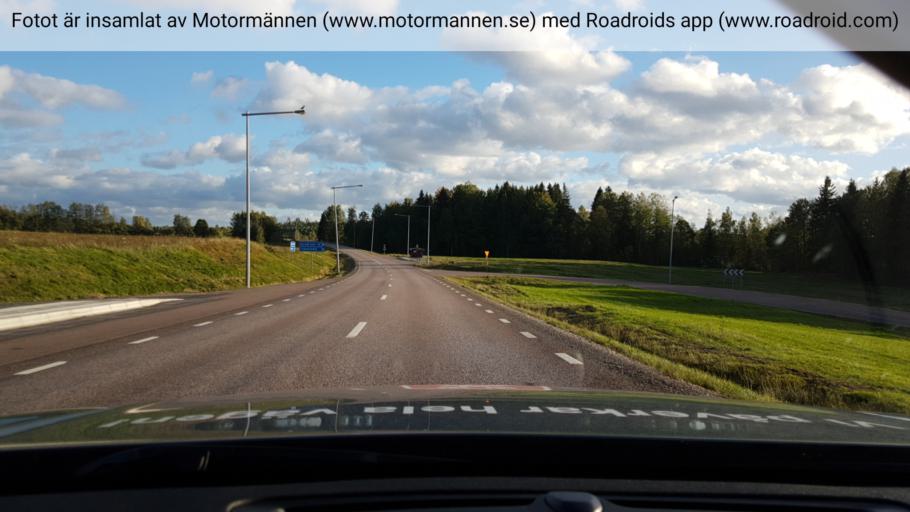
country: SE
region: Vaermland
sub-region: Karlstads Kommun
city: Molkom
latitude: 59.6413
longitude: 13.7158
